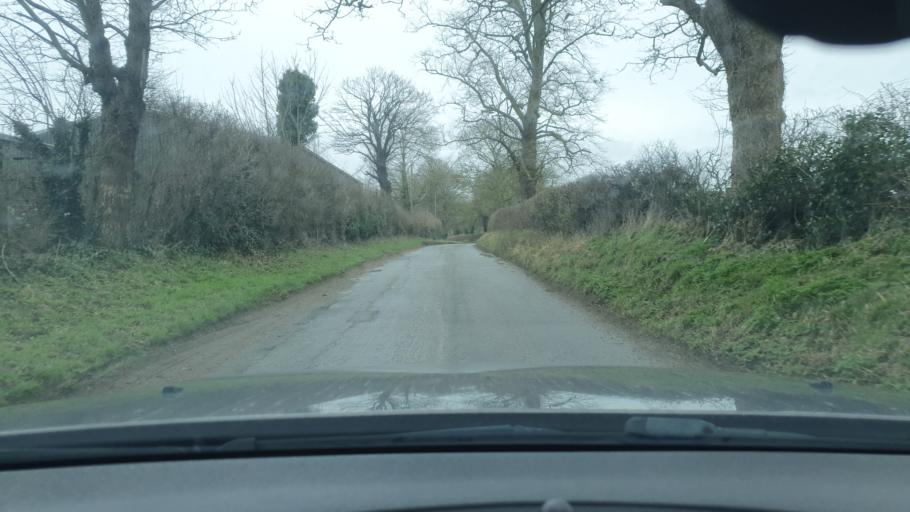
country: GB
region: England
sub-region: West Berkshire
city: Kintbury
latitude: 51.3997
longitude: -1.4648
